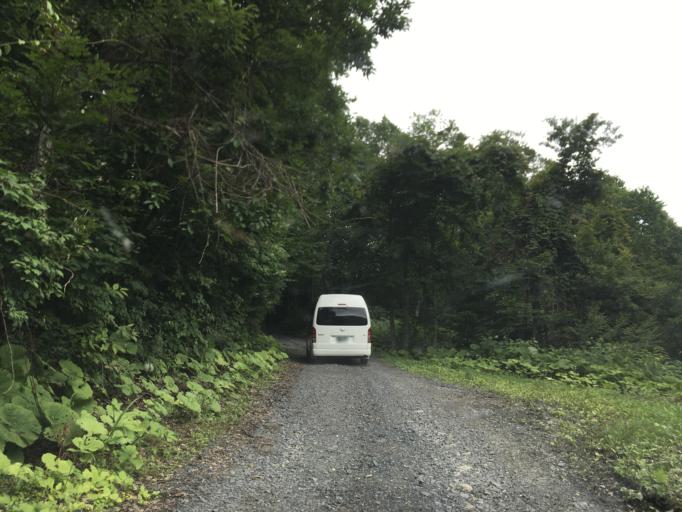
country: JP
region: Iwate
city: Ichinoseki
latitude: 38.9555
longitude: 140.8482
